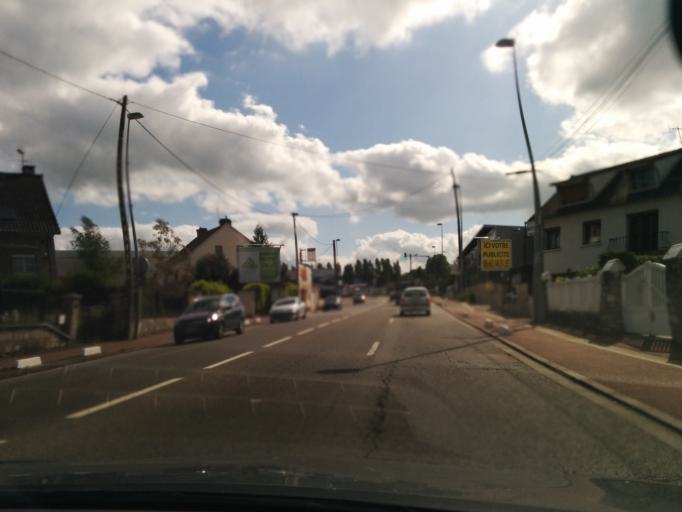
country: FR
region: Ile-de-France
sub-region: Departement des Yvelines
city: Mantes-la-Ville
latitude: 48.9796
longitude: 1.6949
